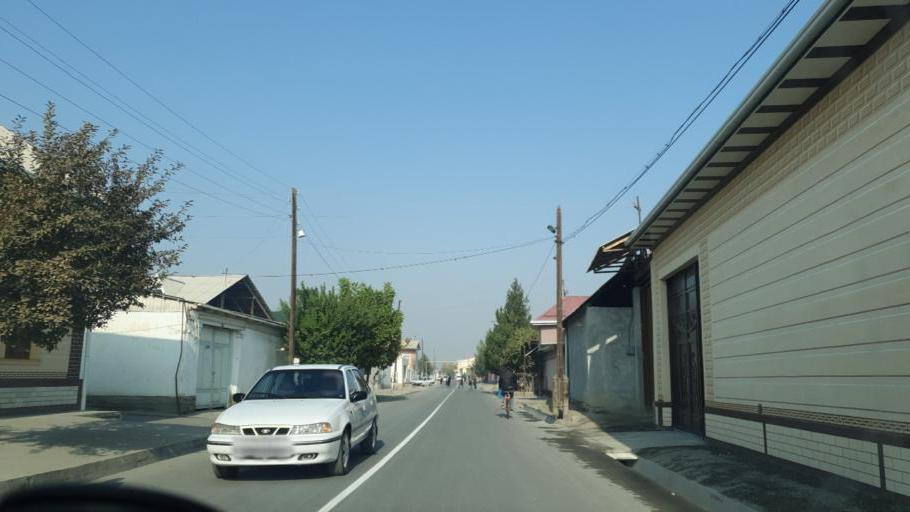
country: UZ
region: Fergana
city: Qo`qon
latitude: 40.5809
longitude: 70.9123
